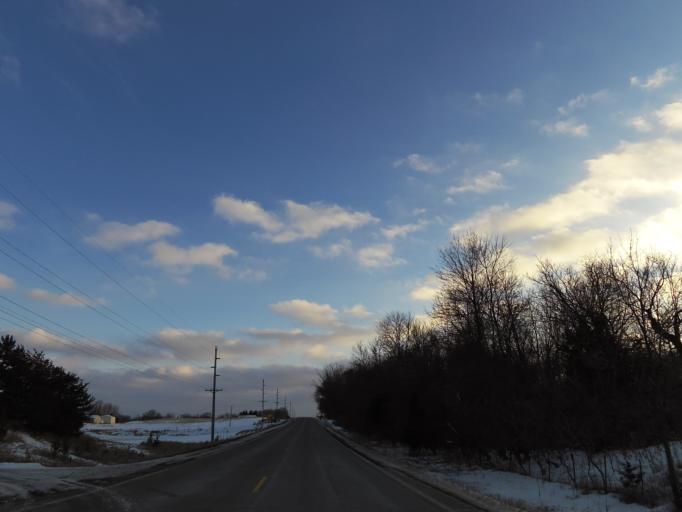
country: US
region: Minnesota
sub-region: Scott County
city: Prior Lake
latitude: 44.6528
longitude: -93.4399
